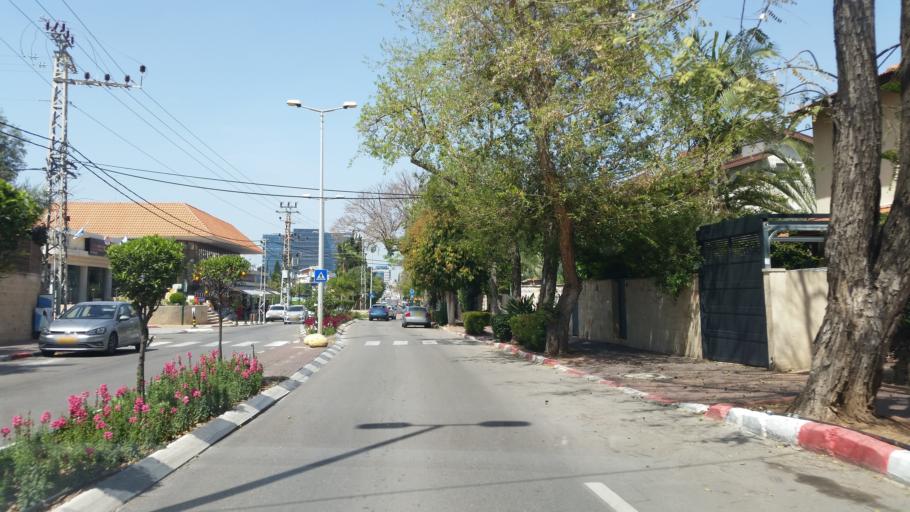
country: IL
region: Central District
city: Ra'anana
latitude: 32.1876
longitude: 34.8830
